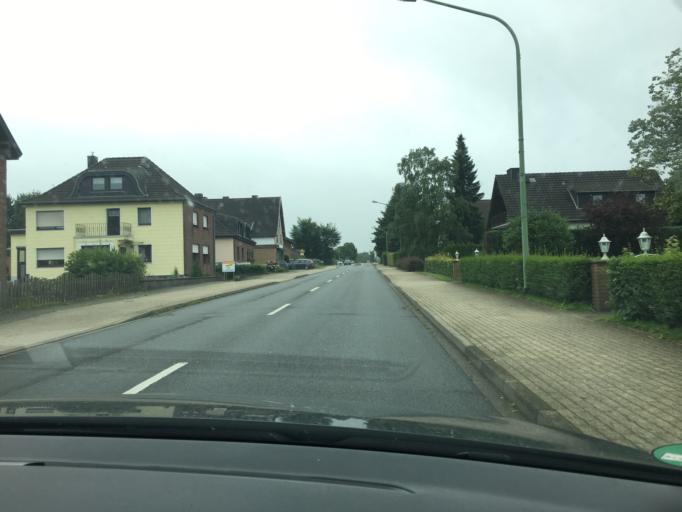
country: DE
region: North Rhine-Westphalia
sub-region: Regierungsbezirk Koln
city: Hurtgenwald
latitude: 50.6879
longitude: 6.3530
